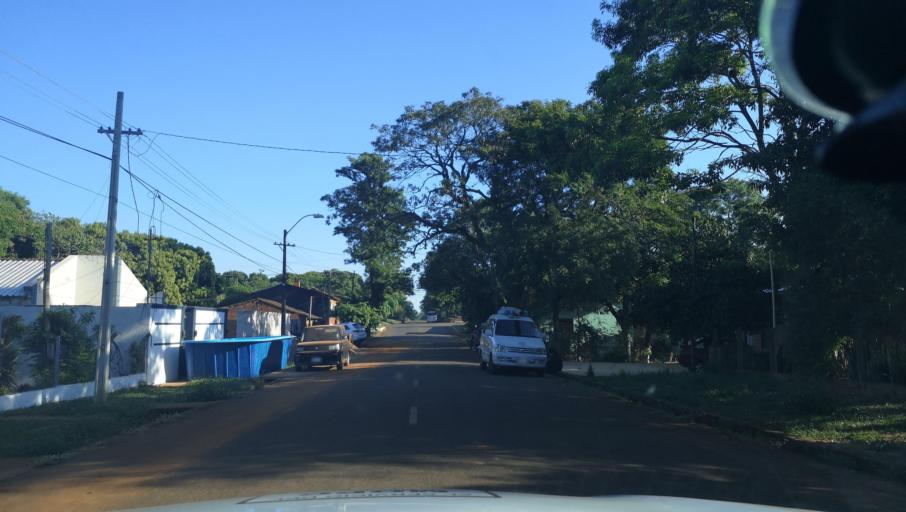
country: PY
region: Itapua
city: Carmen del Parana
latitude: -27.1648
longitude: -56.2431
